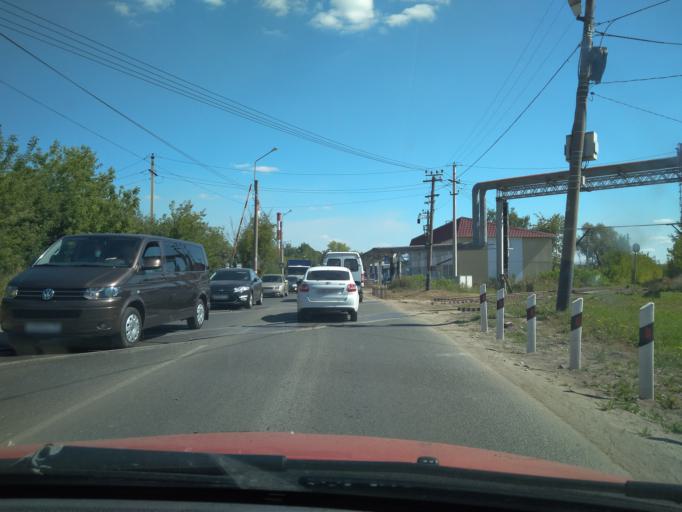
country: RU
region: Mordoviya
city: Saransk
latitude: 54.2084
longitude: 45.1921
